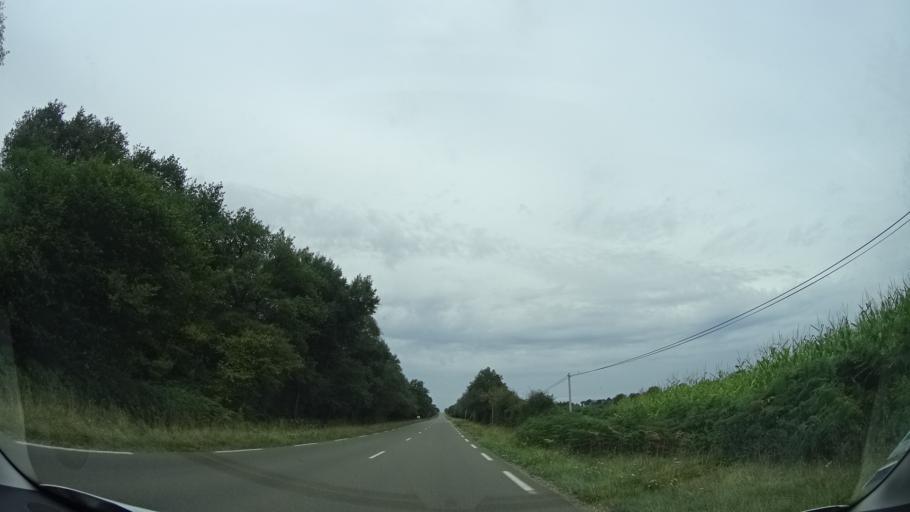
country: FR
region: Pays de la Loire
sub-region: Departement de la Mayenne
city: Meslay-du-Maine
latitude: 47.9879
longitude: -0.6230
